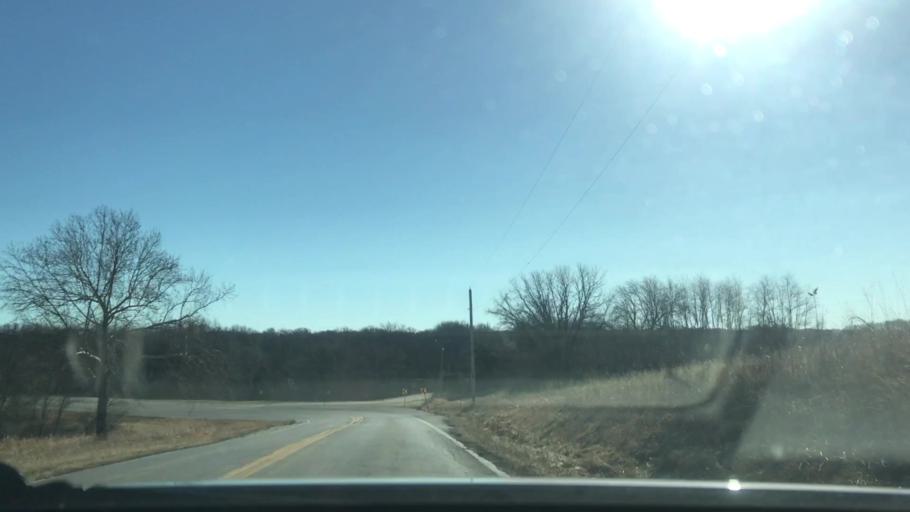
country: US
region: Missouri
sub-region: Platte County
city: Weatherby Lake
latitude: 39.2463
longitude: -94.7603
